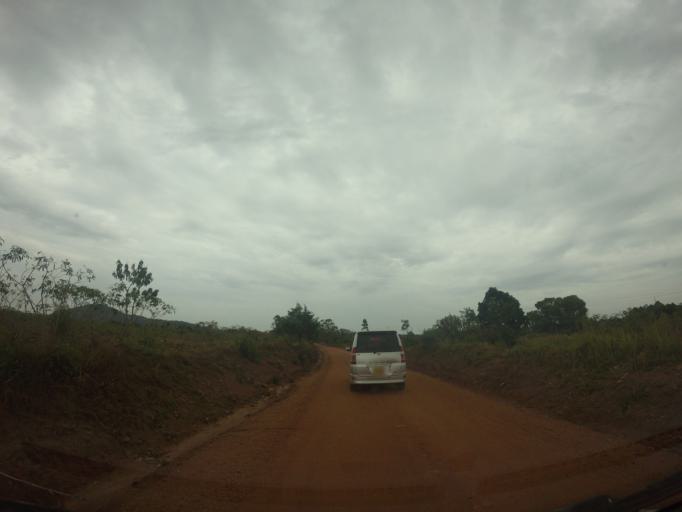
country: UG
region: Northern Region
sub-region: Arua District
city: Arua
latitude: 2.7932
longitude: 30.8707
